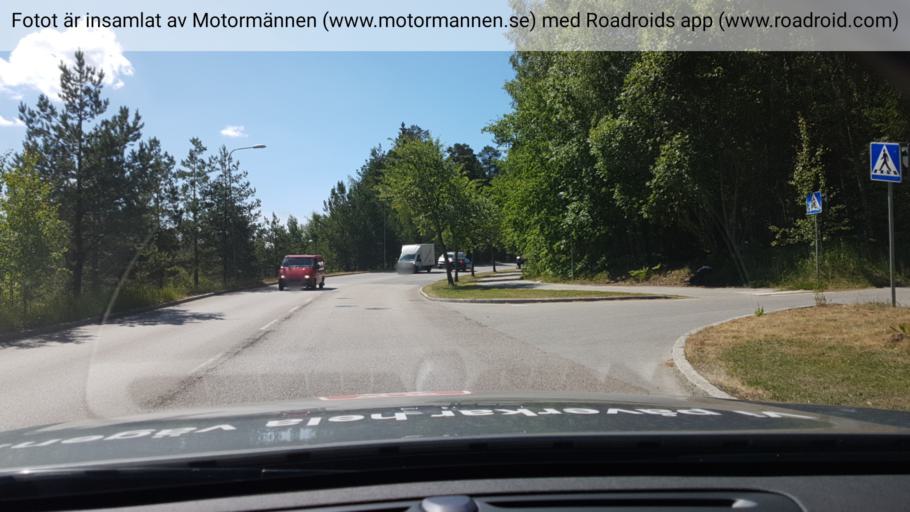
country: SE
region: Stockholm
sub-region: Nacka Kommun
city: Alta
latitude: 59.2349
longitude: 18.1943
